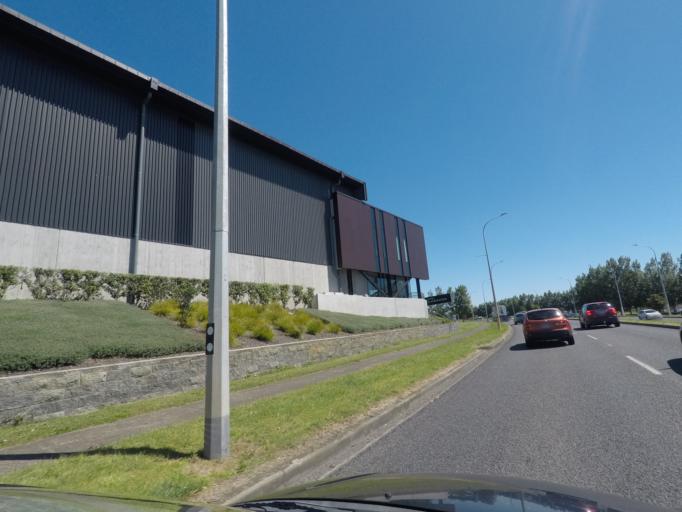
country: NZ
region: Auckland
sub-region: Auckland
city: Tamaki
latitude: -36.9405
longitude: 174.8644
